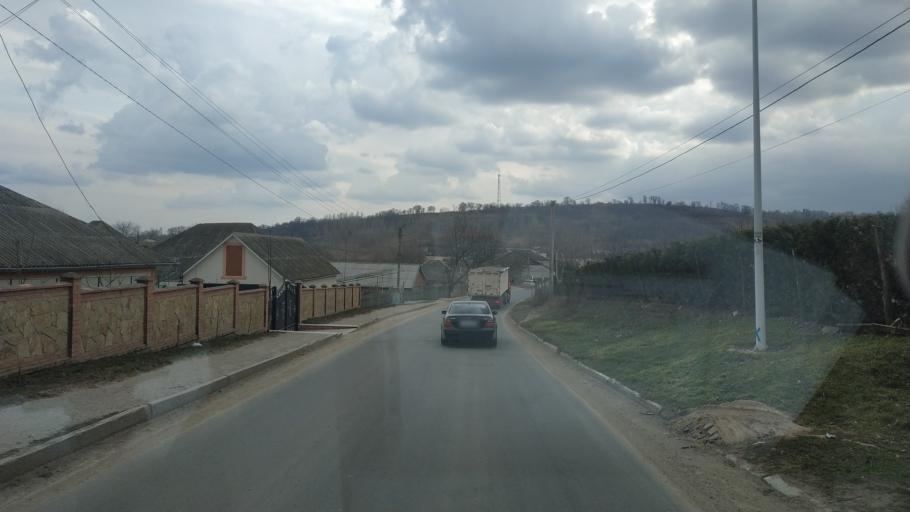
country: MD
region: Anenii Noi
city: Varnita
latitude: 46.8438
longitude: 29.3576
